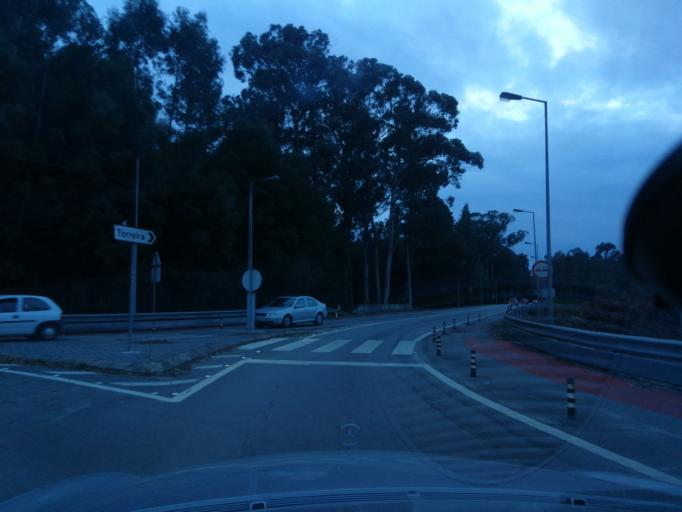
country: PT
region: Aveiro
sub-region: Murtosa
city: Murtosa
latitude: 40.7620
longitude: -8.6332
